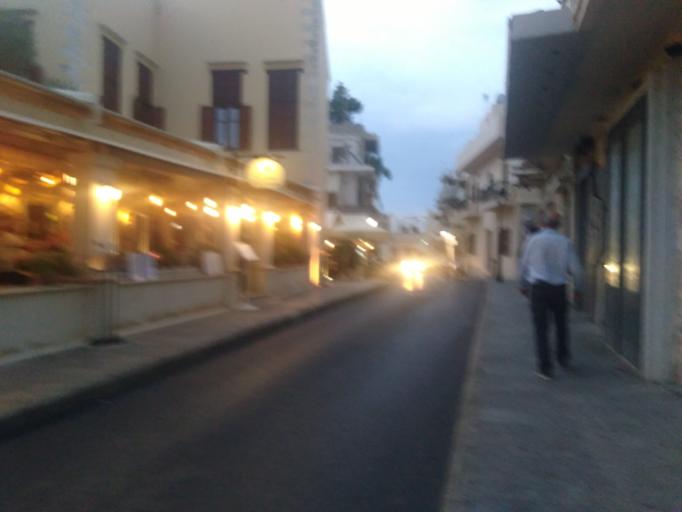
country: GR
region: Crete
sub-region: Nomos Rethymnis
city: Rethymno
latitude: 35.3707
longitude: 24.4748
